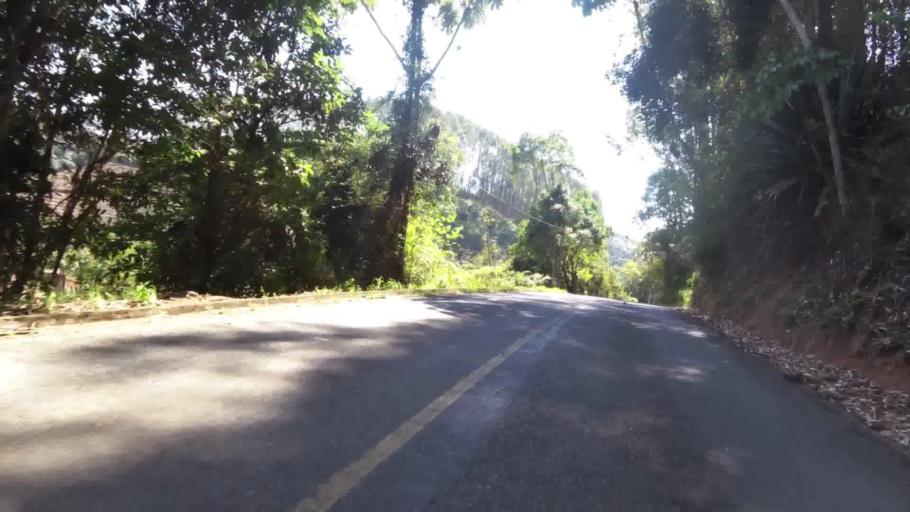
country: BR
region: Espirito Santo
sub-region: Marechal Floriano
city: Marechal Floriano
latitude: -20.4365
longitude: -40.8810
